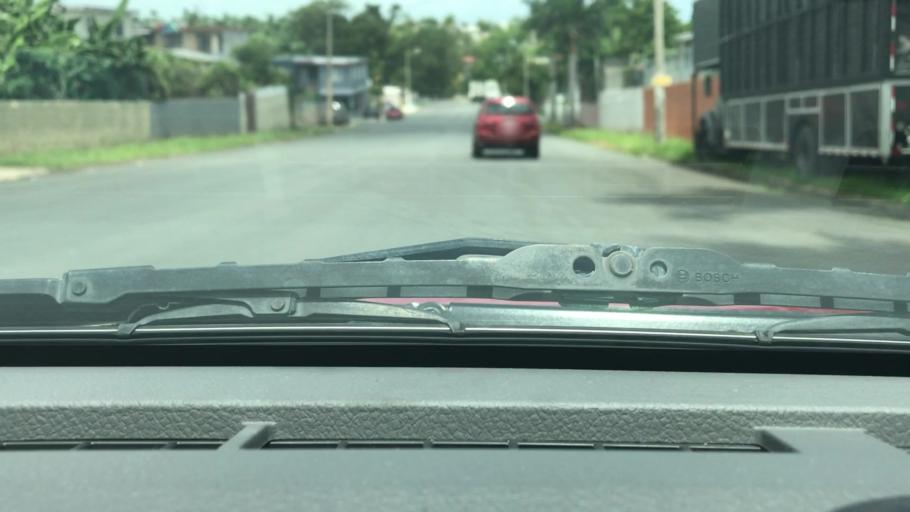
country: PR
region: Toa Alta
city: Pajaros
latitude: 18.3556
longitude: -66.1915
